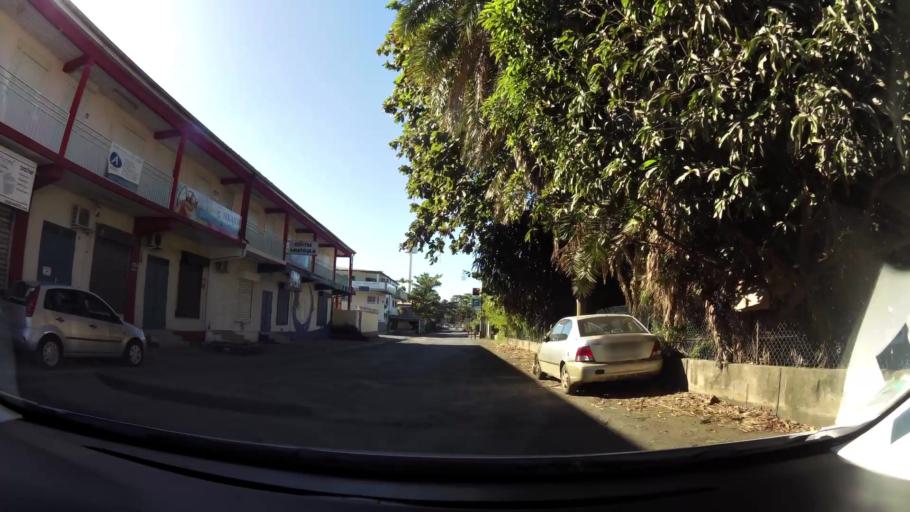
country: YT
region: Mamoudzou
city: Mamoudzou
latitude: -12.7709
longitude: 45.2254
